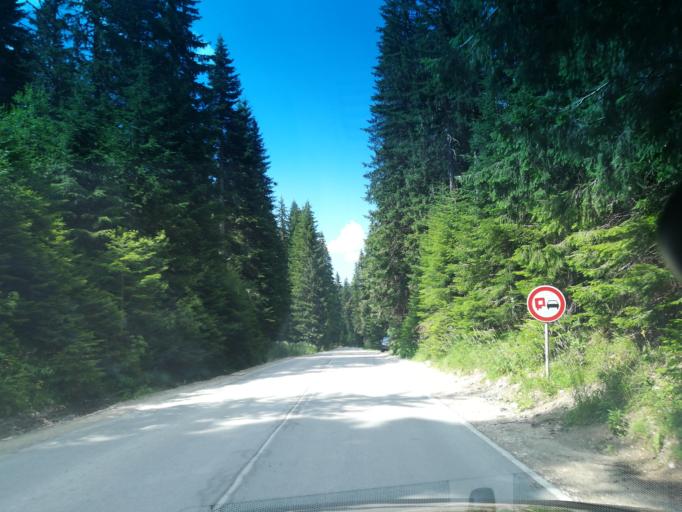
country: BG
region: Smolyan
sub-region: Obshtina Smolyan
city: Smolyan
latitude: 41.6500
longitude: 24.6851
